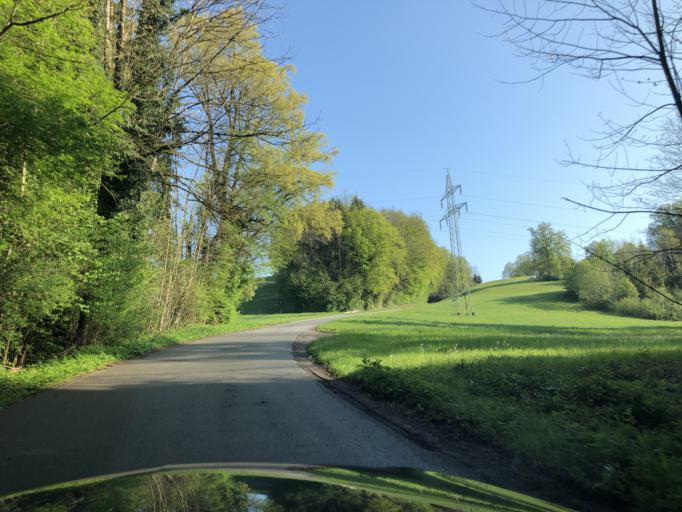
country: DE
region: Bavaria
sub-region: Upper Bavaria
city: Riedering
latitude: 47.8010
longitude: 12.2298
